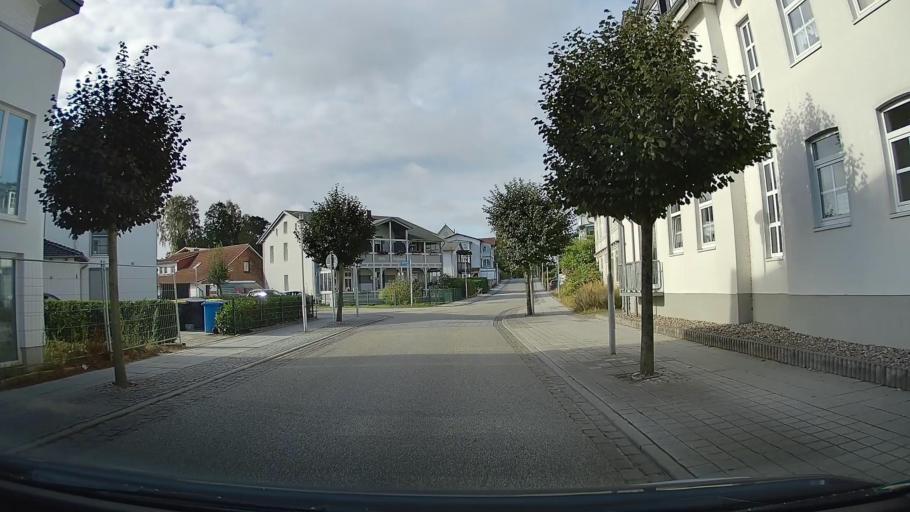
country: DE
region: Mecklenburg-Vorpommern
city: Ostseebad Sellin
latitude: 54.3755
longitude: 13.6897
